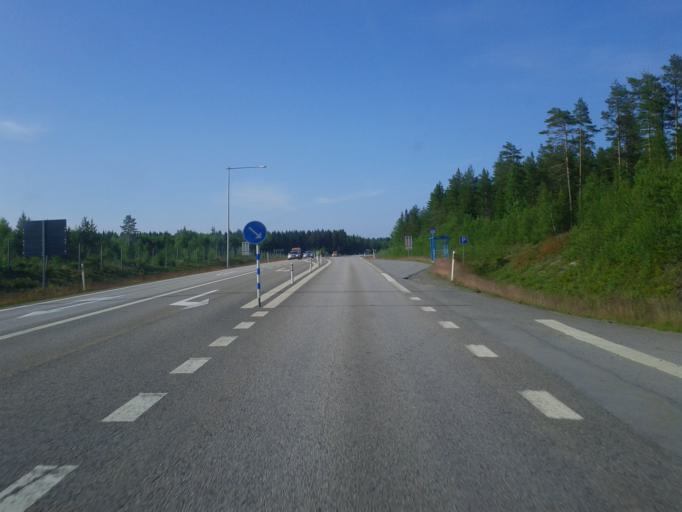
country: SE
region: Vaesterbotten
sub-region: Robertsfors Kommun
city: Robertsfors
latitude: 64.1178
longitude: 20.8814
